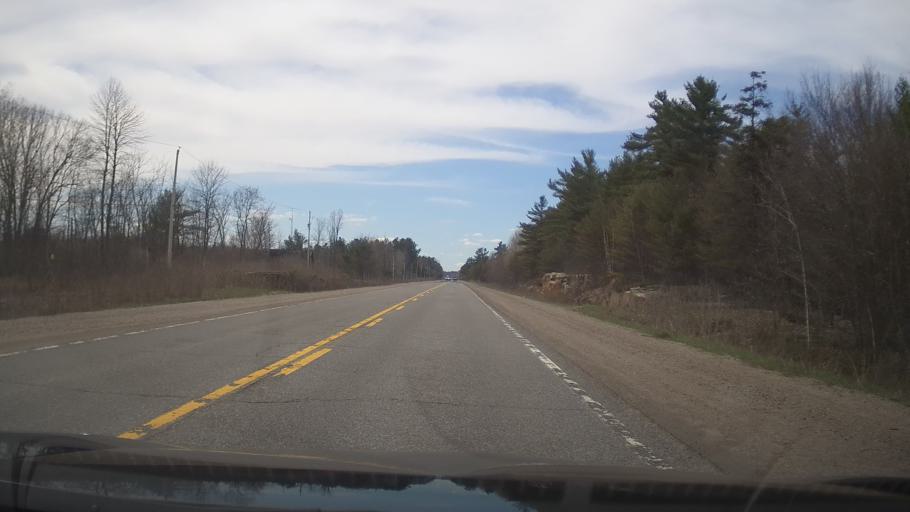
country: CA
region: Ontario
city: Arnprior
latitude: 45.5290
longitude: -76.3048
